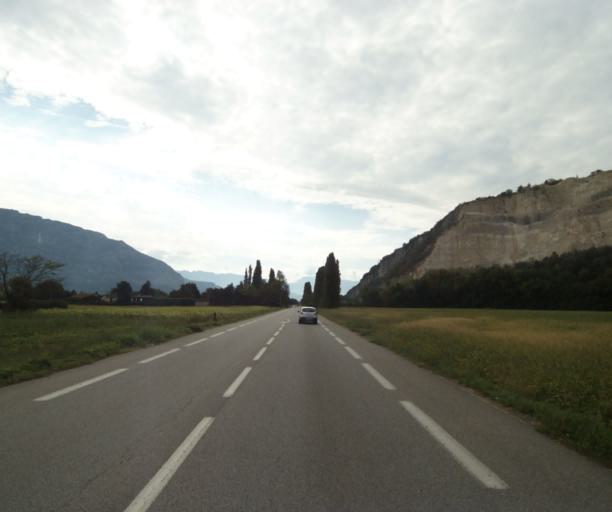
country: FR
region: Rhone-Alpes
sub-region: Departement de l'Isere
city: Noyarey
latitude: 45.2349
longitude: 5.6406
